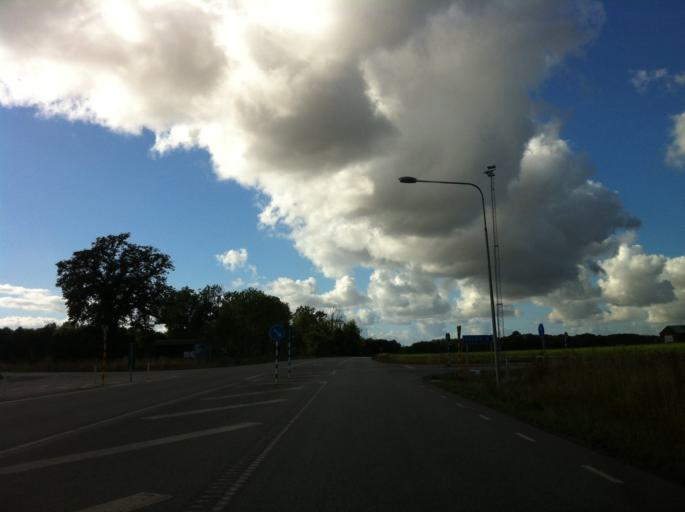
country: SE
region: Skane
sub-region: Eslovs Kommun
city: Eslov
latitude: 55.7861
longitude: 13.2624
